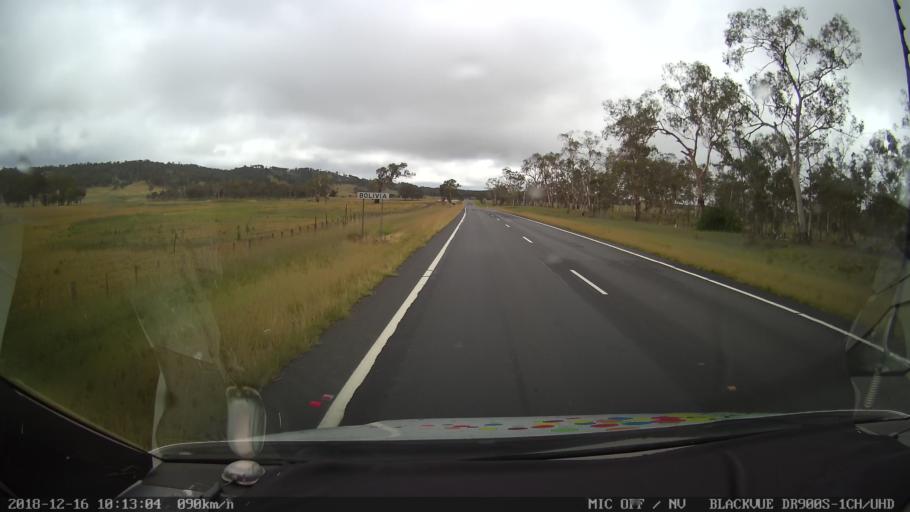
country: AU
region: New South Wales
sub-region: Glen Innes Severn
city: Glen Innes
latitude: -29.3005
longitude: 151.9484
